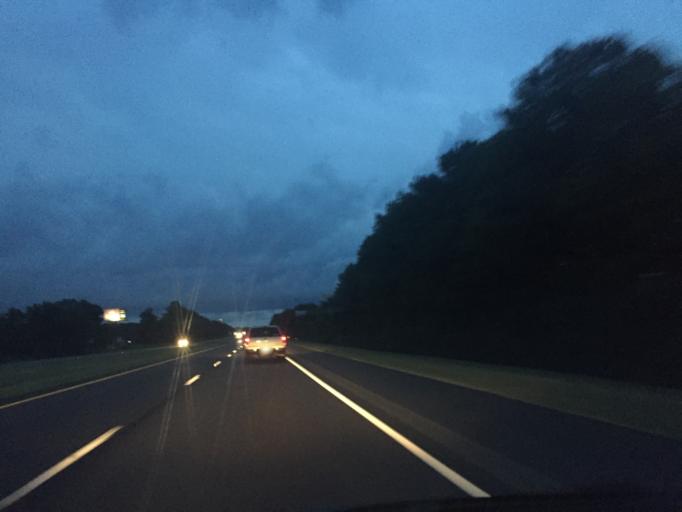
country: US
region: Georgia
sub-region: Chatham County
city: Georgetown
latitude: 32.0017
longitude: -81.2640
